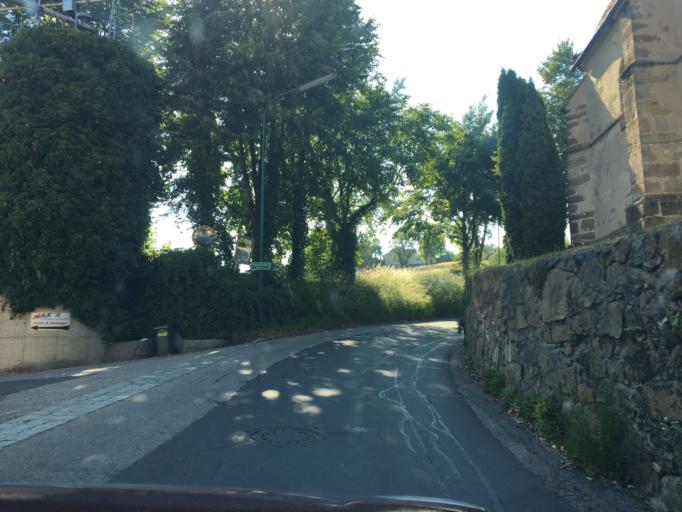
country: AT
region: Lower Austria
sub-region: Politischer Bezirk Amstetten
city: Ennsdorf
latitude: 48.2670
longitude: 14.5486
